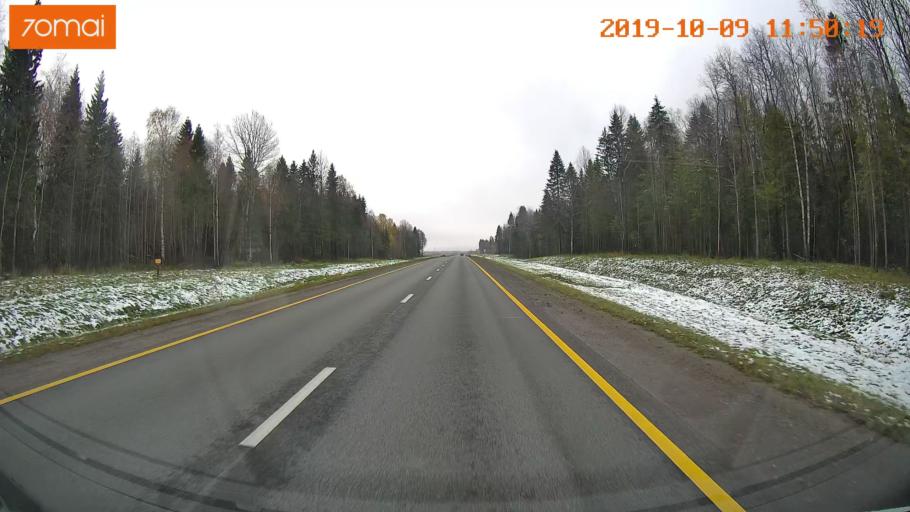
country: RU
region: Vologda
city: Gryazovets
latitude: 58.8070
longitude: 40.2446
